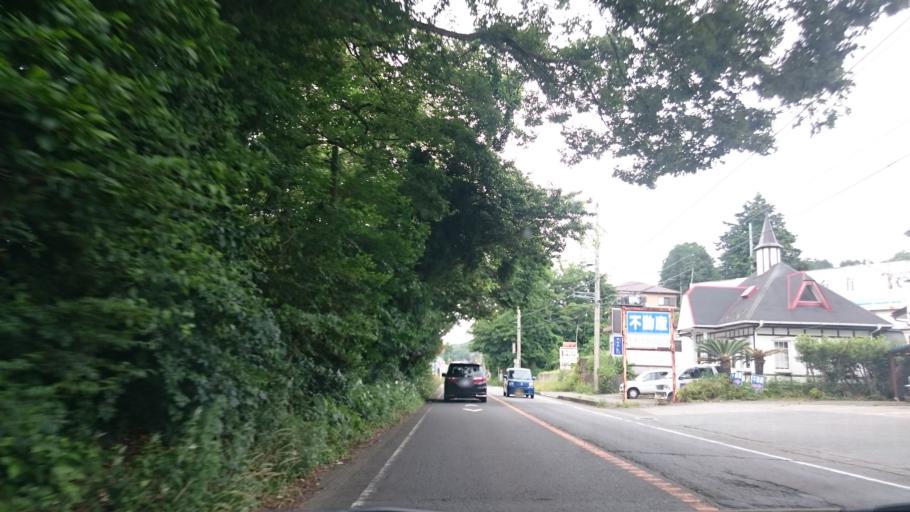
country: JP
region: Shizuoka
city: Ito
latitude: 34.9171
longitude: 139.1206
